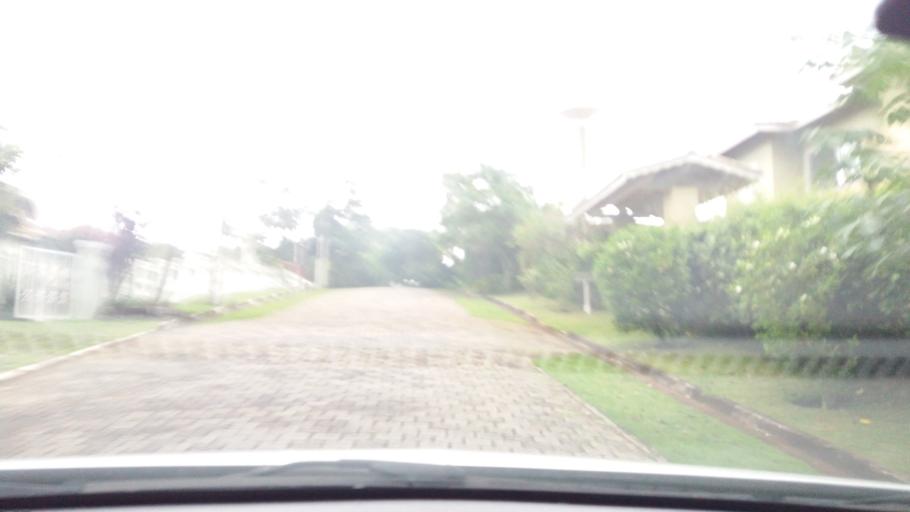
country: BR
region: Sao Paulo
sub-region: Bom Jesus Dos Perdoes
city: Bom Jesus dos Perdoes
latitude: -23.1659
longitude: -46.4621
